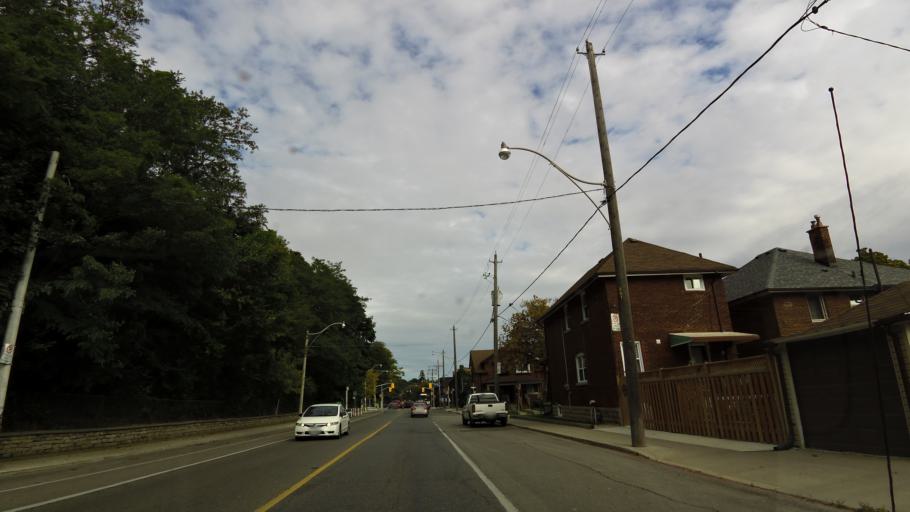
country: CA
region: Ontario
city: Toronto
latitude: 43.6752
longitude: -79.4247
